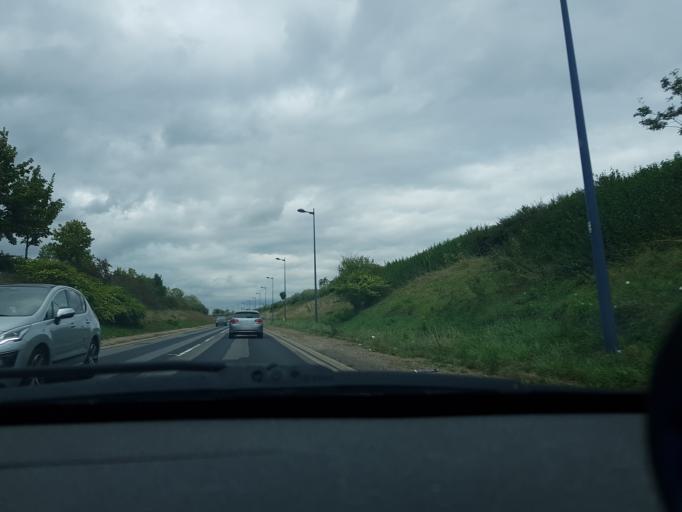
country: FR
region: Lorraine
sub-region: Departement de Meurthe-et-Moselle
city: Saulxures-les-Nancy
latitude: 48.6872
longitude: 6.2332
